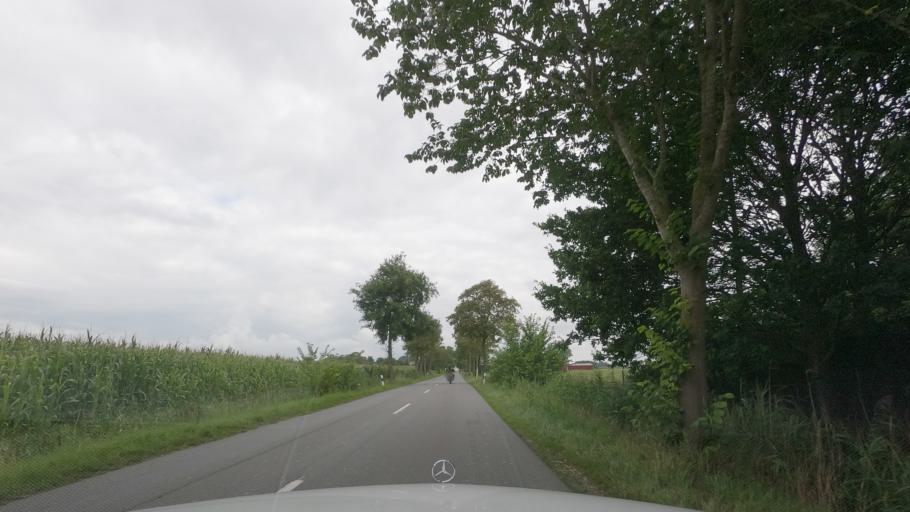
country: DE
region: Lower Saxony
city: Uthlede
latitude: 53.2907
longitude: 8.5312
